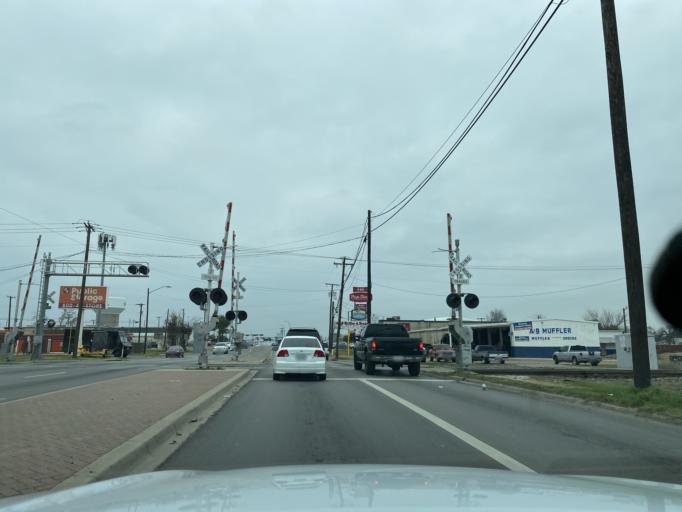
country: US
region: Texas
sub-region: Tarrant County
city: Arlington
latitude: 32.7367
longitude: -97.0973
